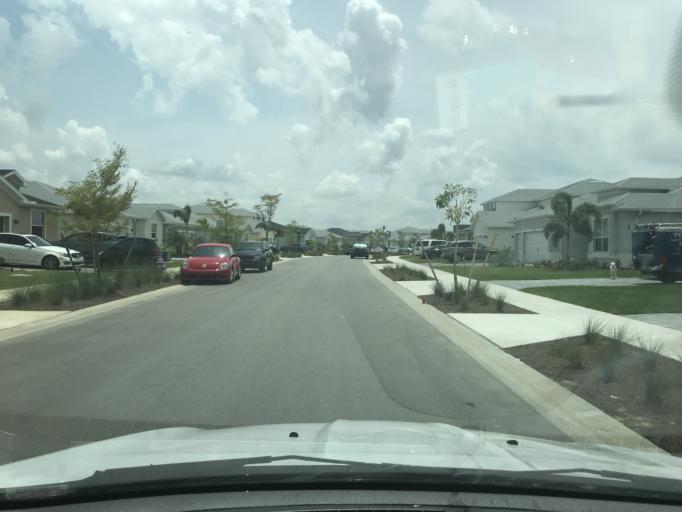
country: US
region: Florida
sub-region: Lee County
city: Olga
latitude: 26.7790
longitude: -81.7379
